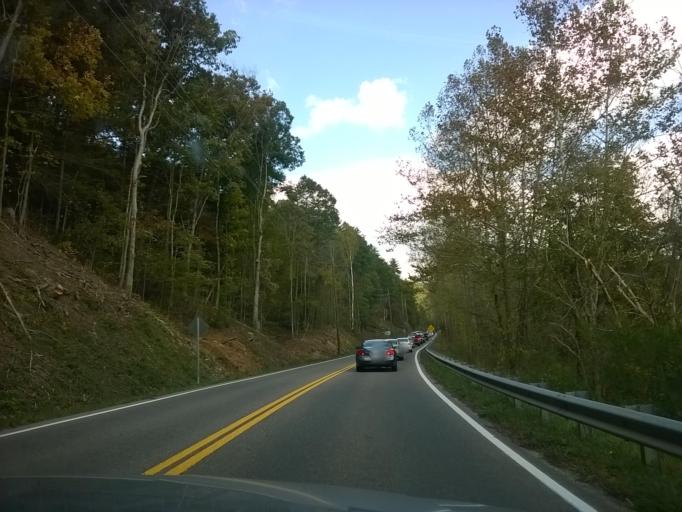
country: US
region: Tennessee
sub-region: Sevier County
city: Pigeon Forge
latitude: 35.7506
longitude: -83.6276
